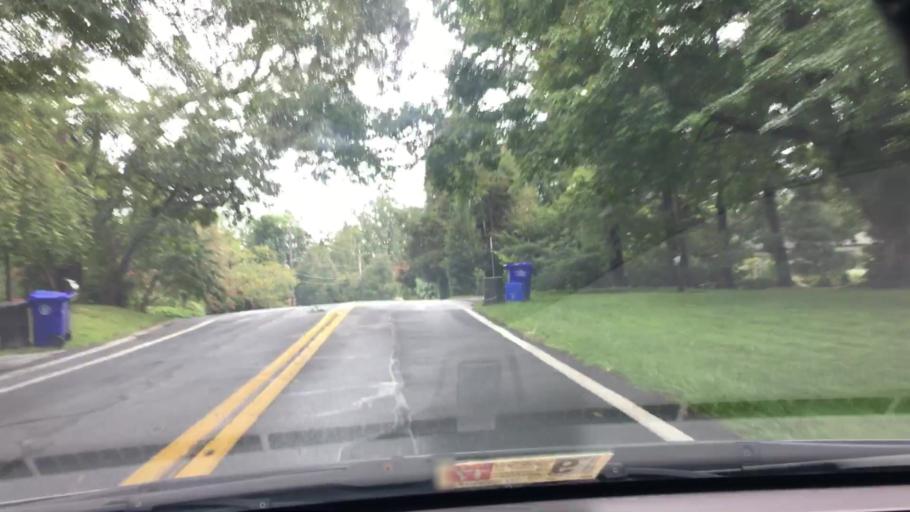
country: US
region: Maryland
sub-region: Montgomery County
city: Cabin John
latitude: 38.9852
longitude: -77.1732
